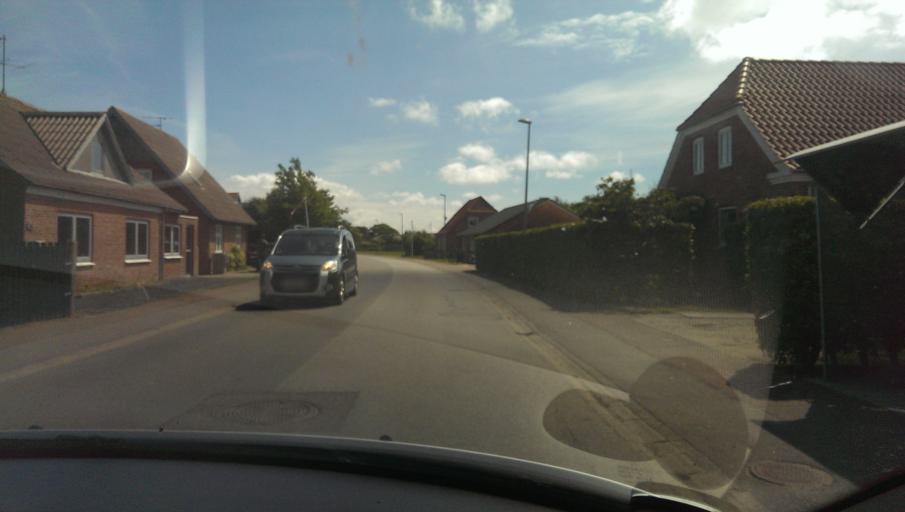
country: DK
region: Central Jutland
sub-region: Ringkobing-Skjern Kommune
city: Ringkobing
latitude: 56.1237
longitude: 8.1767
